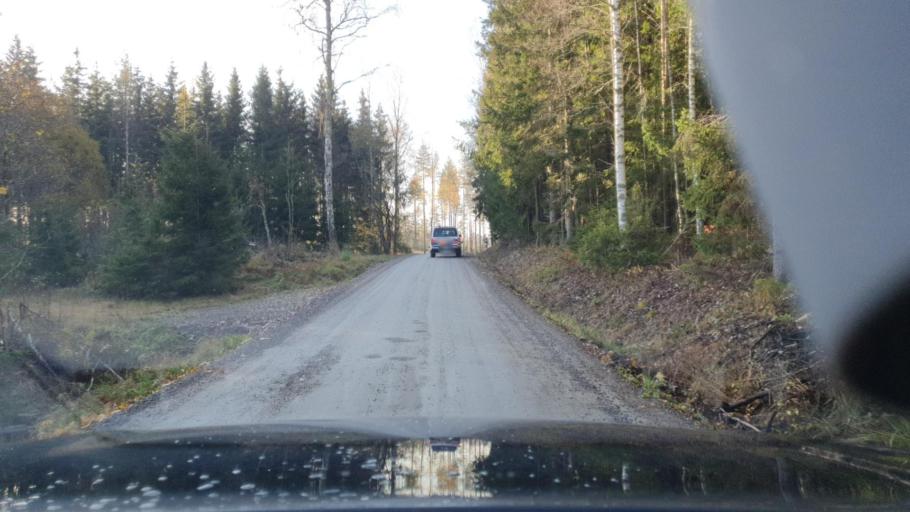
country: SE
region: Vaermland
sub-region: Grums Kommun
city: Slottsbron
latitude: 59.4617
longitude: 12.9191
